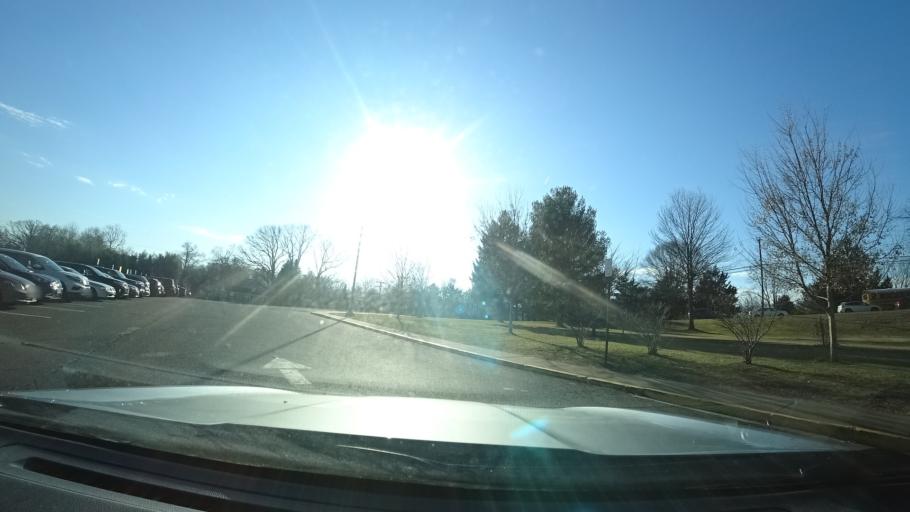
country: US
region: Virginia
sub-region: Fairfax County
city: Herndon
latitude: 38.9762
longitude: -77.3777
